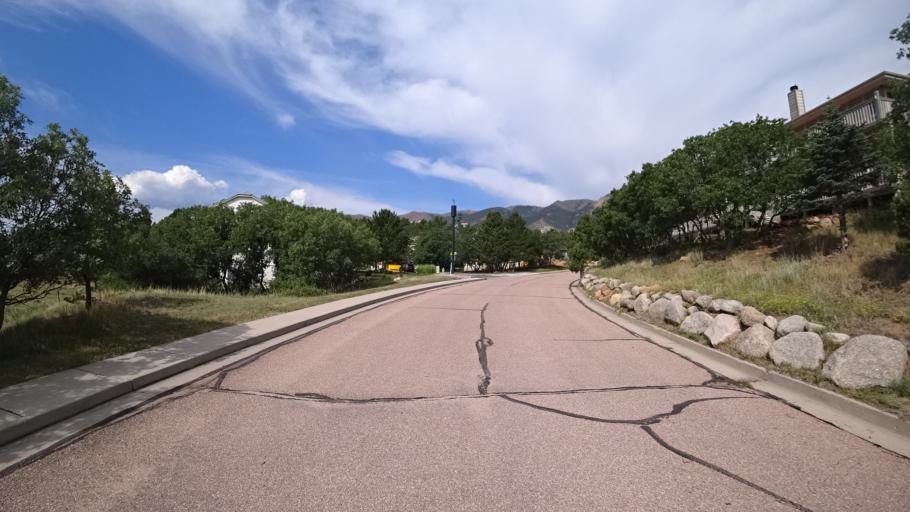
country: US
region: Colorado
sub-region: El Paso County
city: Air Force Academy
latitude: 38.9518
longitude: -104.8681
